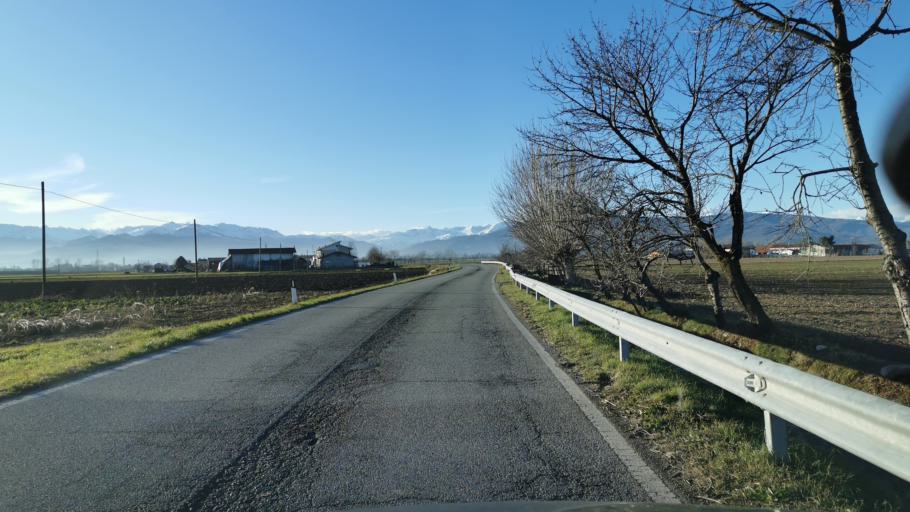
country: IT
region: Piedmont
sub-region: Provincia di Cuneo
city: Roata Rossi
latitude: 44.4574
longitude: 7.5151
